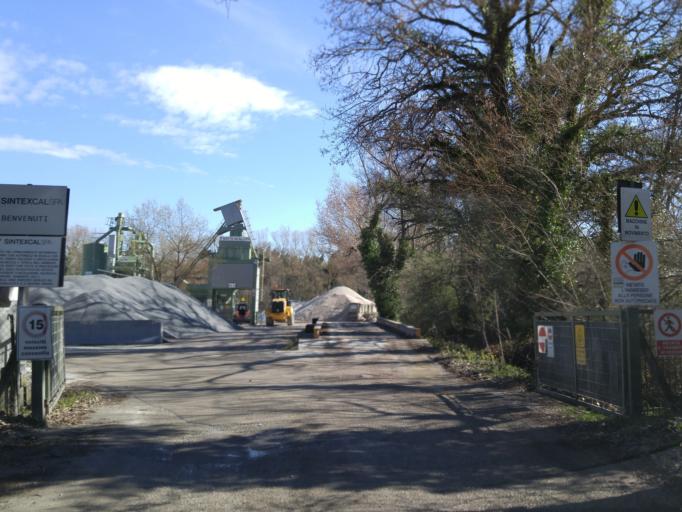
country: IT
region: The Marches
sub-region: Provincia di Pesaro e Urbino
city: Calcinelli
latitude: 43.7413
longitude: 12.9162
